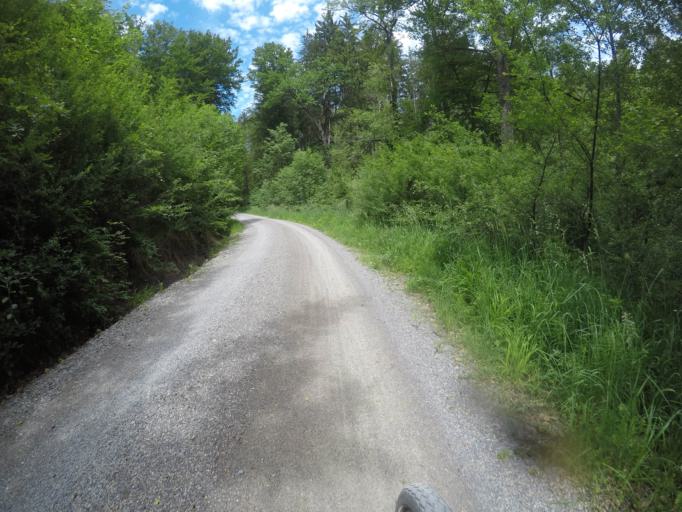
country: DE
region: Baden-Wuerttemberg
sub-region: Regierungsbezirk Stuttgart
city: Hildrizhausen
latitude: 48.6012
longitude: 8.9813
